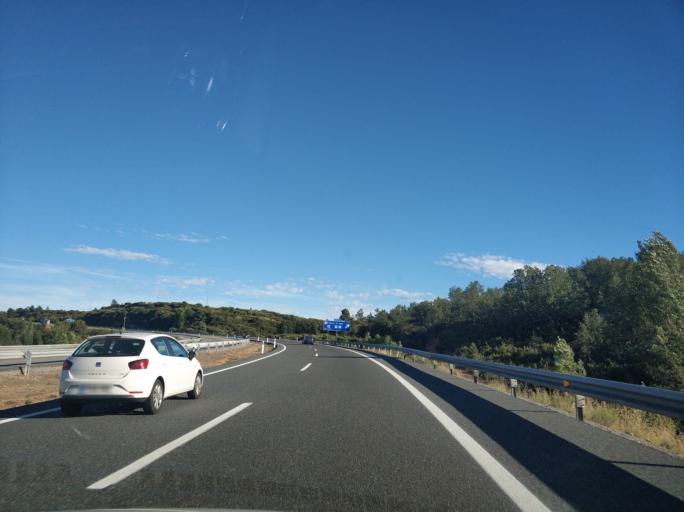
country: ES
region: Castille and Leon
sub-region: Provincia de Leon
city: Santa Maria de Ordas
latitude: 42.6998
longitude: -5.7812
